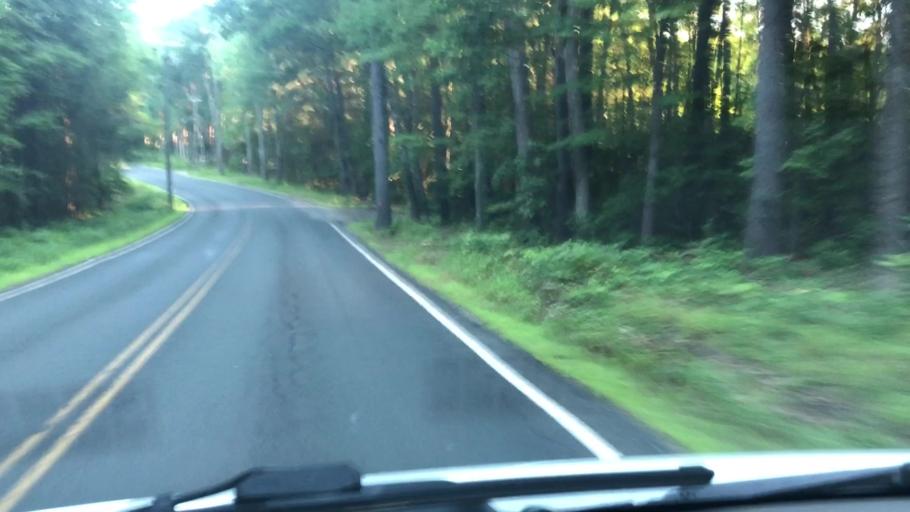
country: US
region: Massachusetts
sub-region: Hampshire County
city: Westhampton
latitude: 42.2787
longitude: -72.7528
